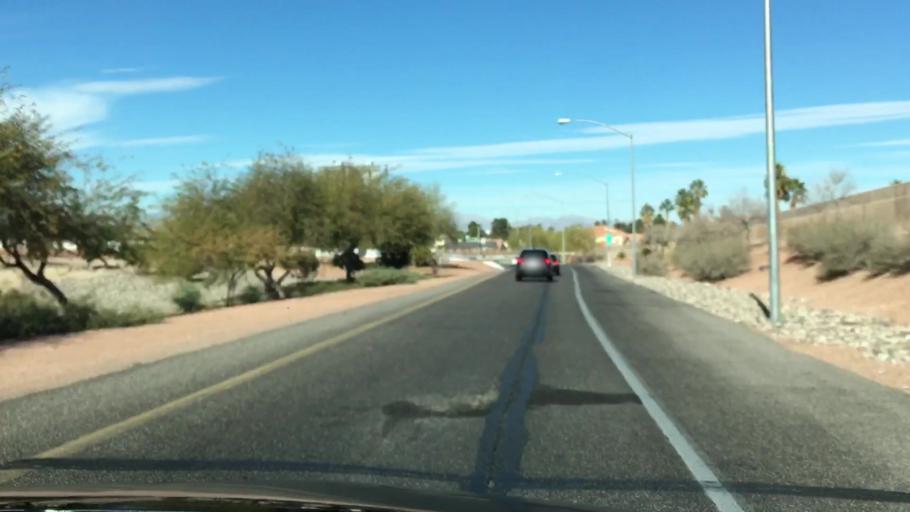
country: US
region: Nevada
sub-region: Clark County
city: Paradise
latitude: 36.0554
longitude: -115.1380
